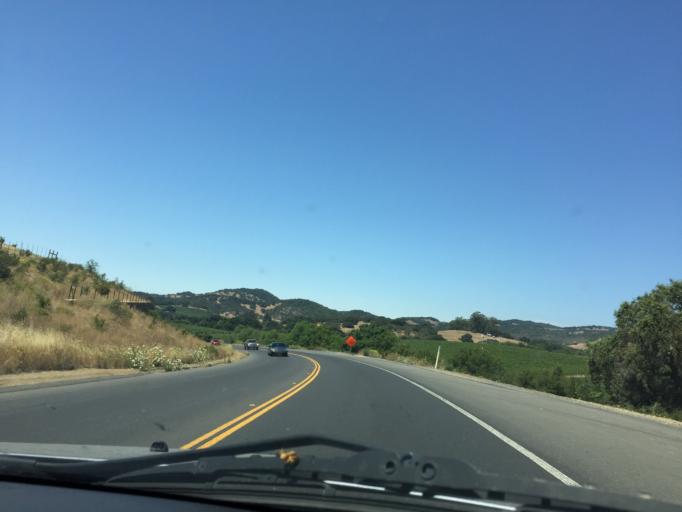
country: US
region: California
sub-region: Napa County
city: Napa
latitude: 38.2582
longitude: -122.3558
